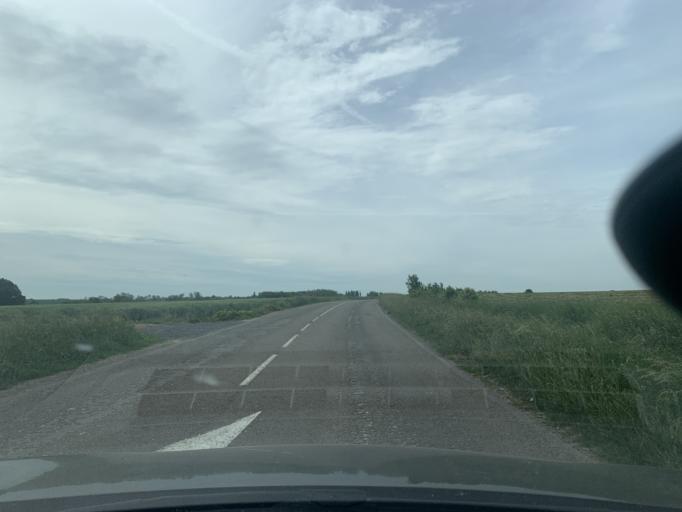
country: FR
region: Nord-Pas-de-Calais
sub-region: Departement du Nord
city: Marcoing
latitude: 50.1334
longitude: 3.1832
